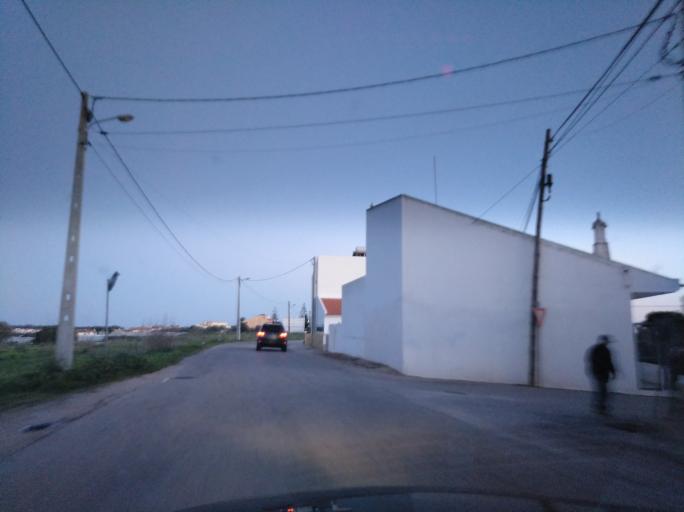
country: PT
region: Faro
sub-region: Vila Real de Santo Antonio
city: Monte Gordo
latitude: 37.1841
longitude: -7.5068
